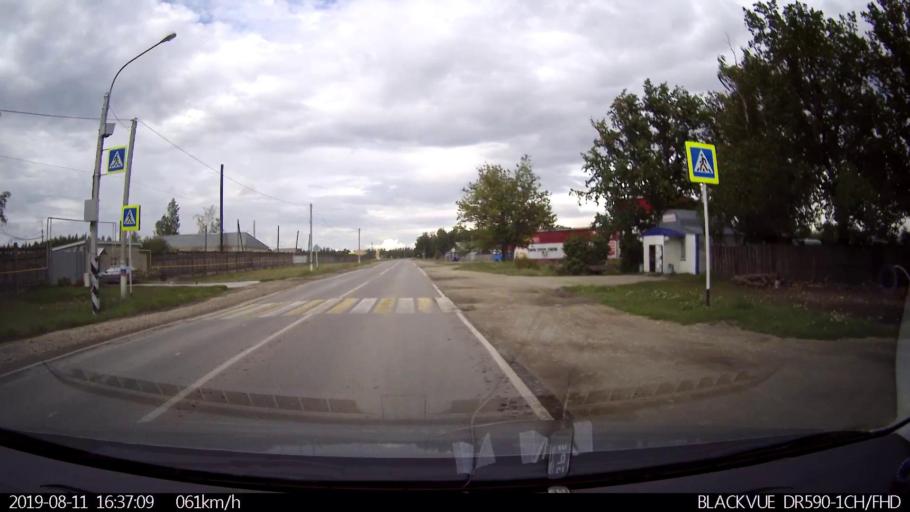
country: RU
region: Ulyanovsk
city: Mayna
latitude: 54.1249
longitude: 47.6125
